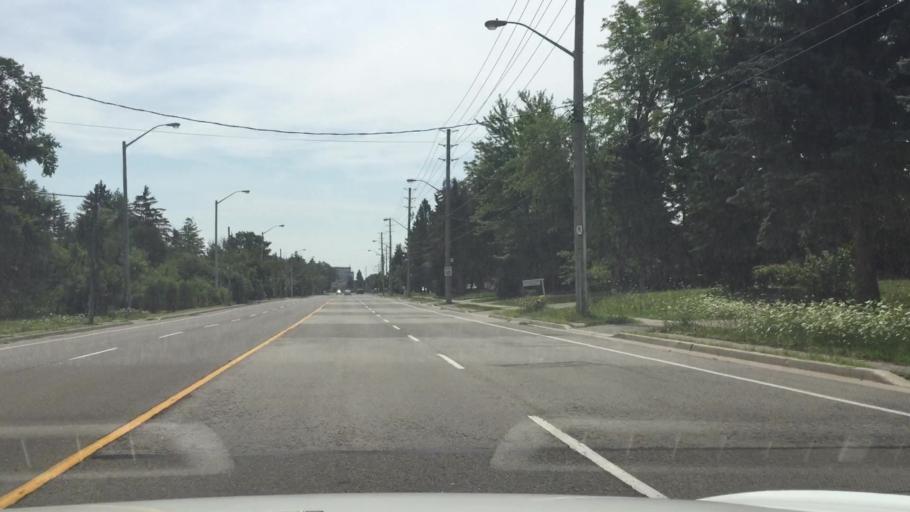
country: CA
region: Ontario
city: Pickering
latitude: 43.8056
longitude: -79.1601
